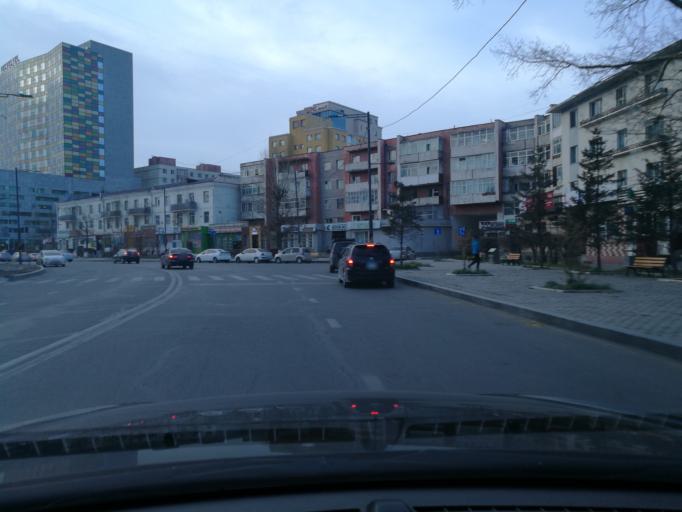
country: MN
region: Ulaanbaatar
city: Ulaanbaatar
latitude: 47.9261
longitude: 106.9197
